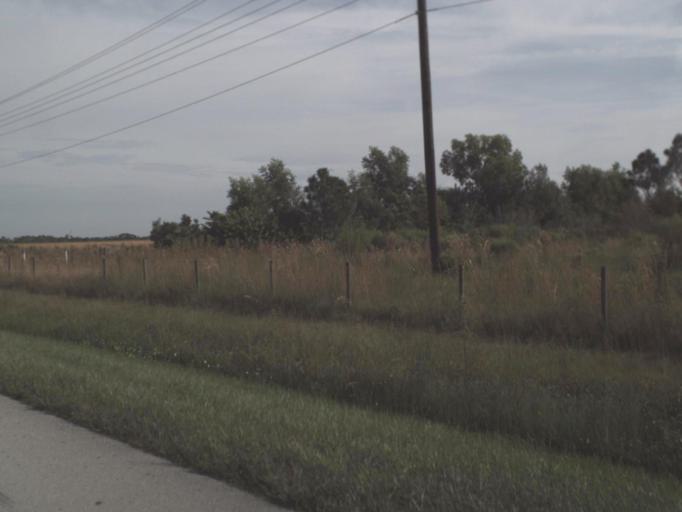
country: US
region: Florida
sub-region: Lee County
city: Fort Myers Shores
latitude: 26.7543
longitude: -81.7609
